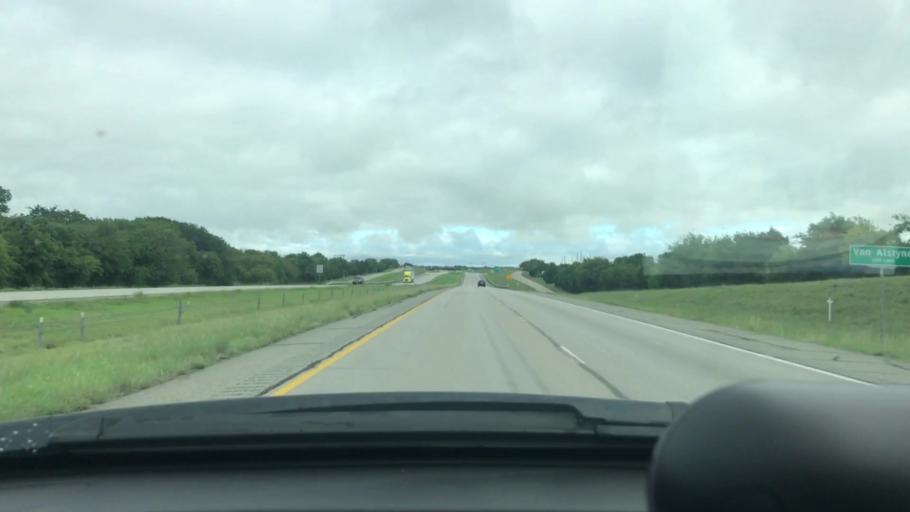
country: US
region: Texas
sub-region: Grayson County
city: Van Alstyne
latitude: 33.3911
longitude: -96.5804
